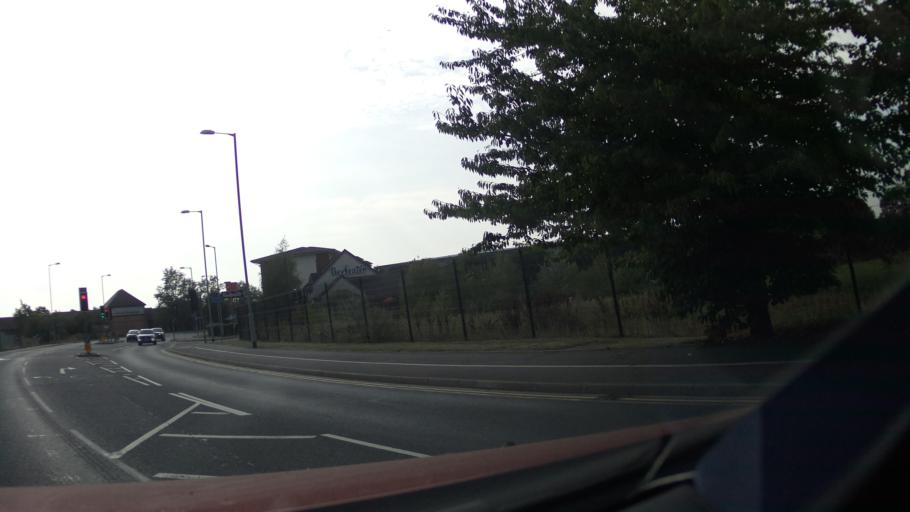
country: GB
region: England
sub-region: Staffordshire
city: Burton upon Trent
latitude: 52.7959
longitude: -1.6598
